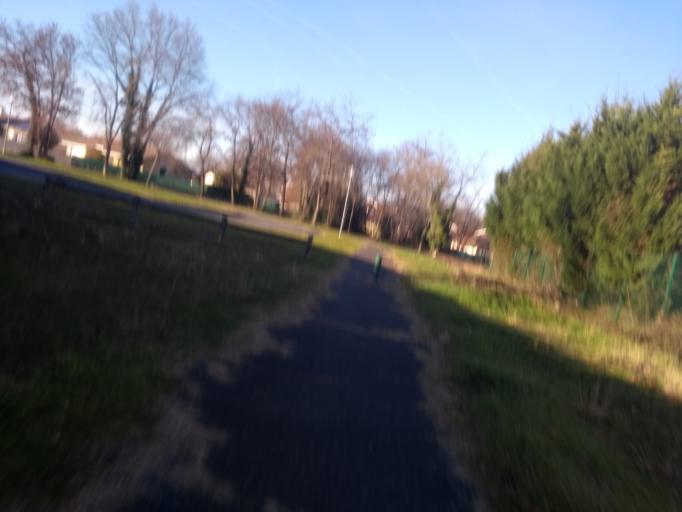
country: FR
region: Aquitaine
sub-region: Departement de la Gironde
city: Le Barp
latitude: 44.6048
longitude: -0.7724
